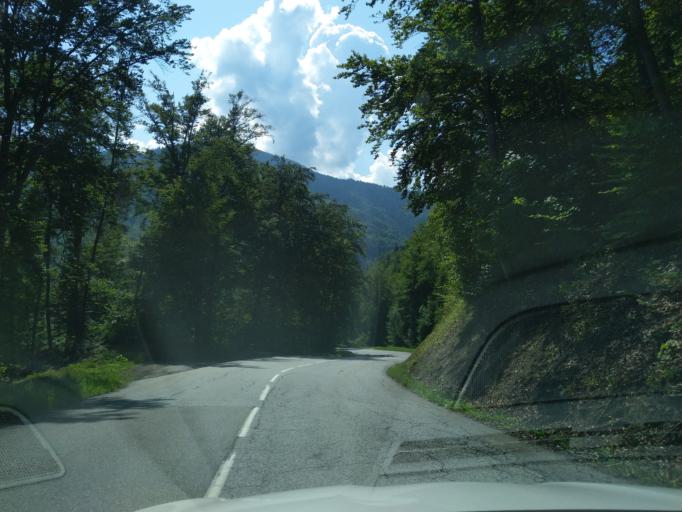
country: FR
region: Rhone-Alpes
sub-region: Departement de la Savoie
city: Les Allues
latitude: 45.4491
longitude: 6.5586
